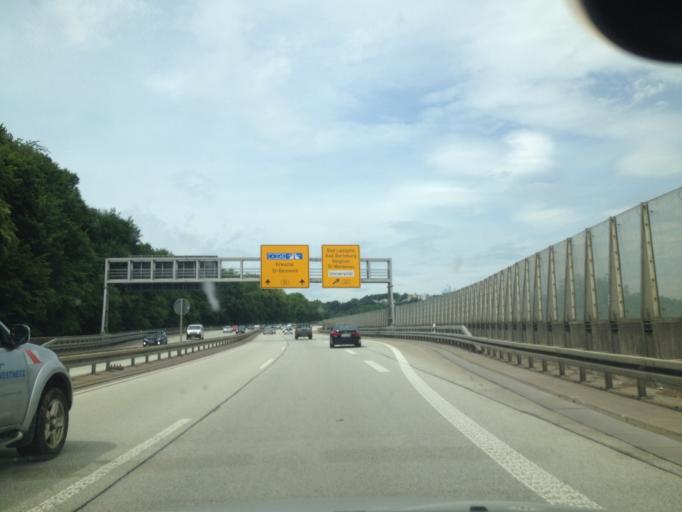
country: DE
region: North Rhine-Westphalia
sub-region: Regierungsbezirk Arnsberg
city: Siegen
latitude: 50.8937
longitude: 8.0233
